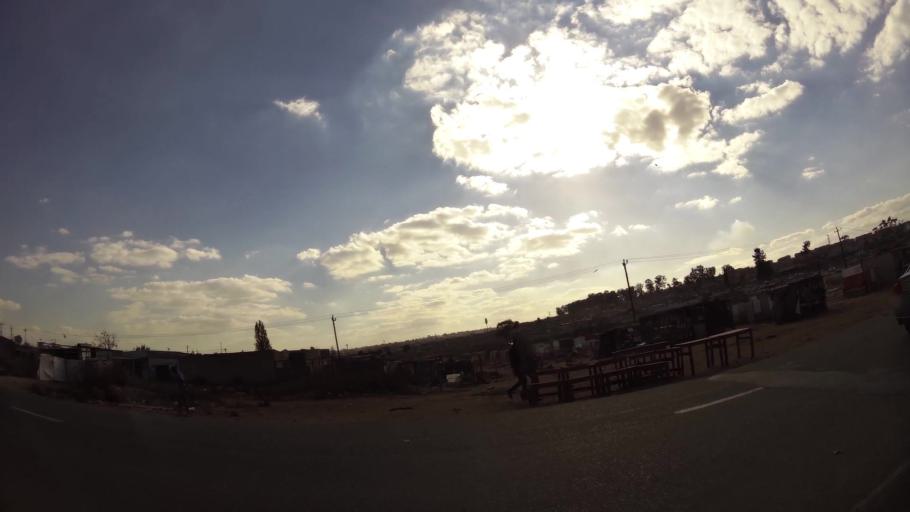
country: ZA
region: Gauteng
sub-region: Ekurhuleni Metropolitan Municipality
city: Tembisa
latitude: -25.9911
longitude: 28.1904
